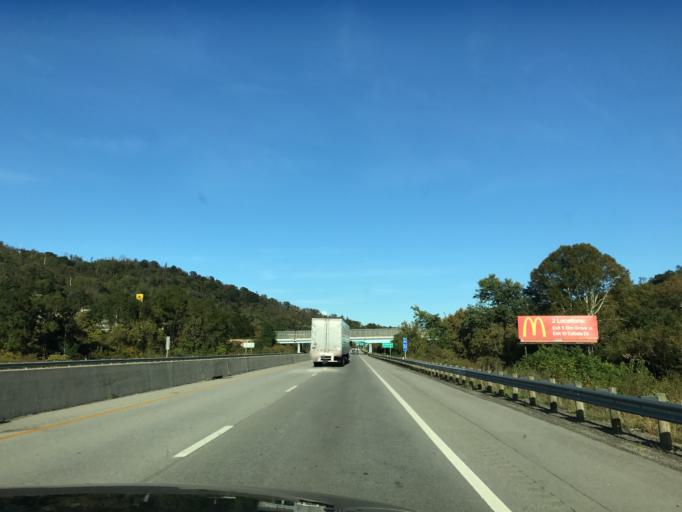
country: US
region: Ohio
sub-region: Belmont County
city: Bridgeport
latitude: 40.0692
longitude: -80.7564
